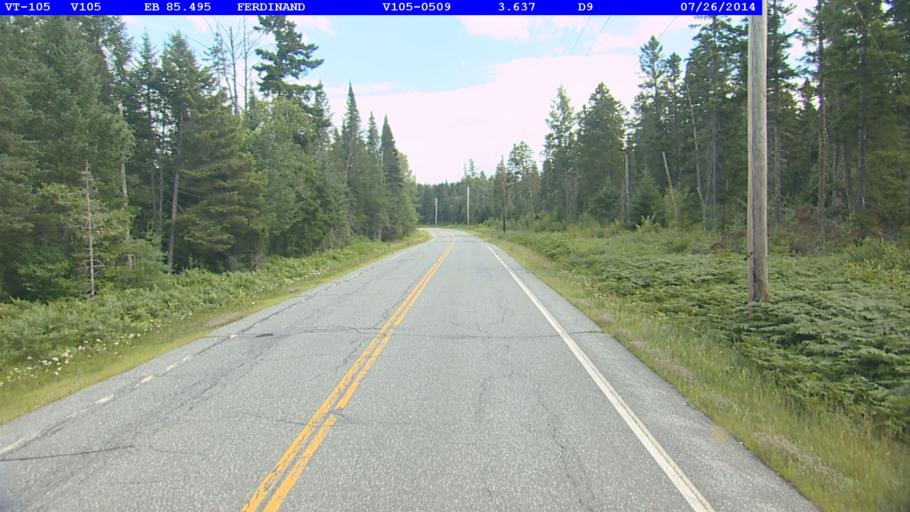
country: US
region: New Hampshire
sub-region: Coos County
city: Stratford
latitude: 44.7680
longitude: -71.7385
